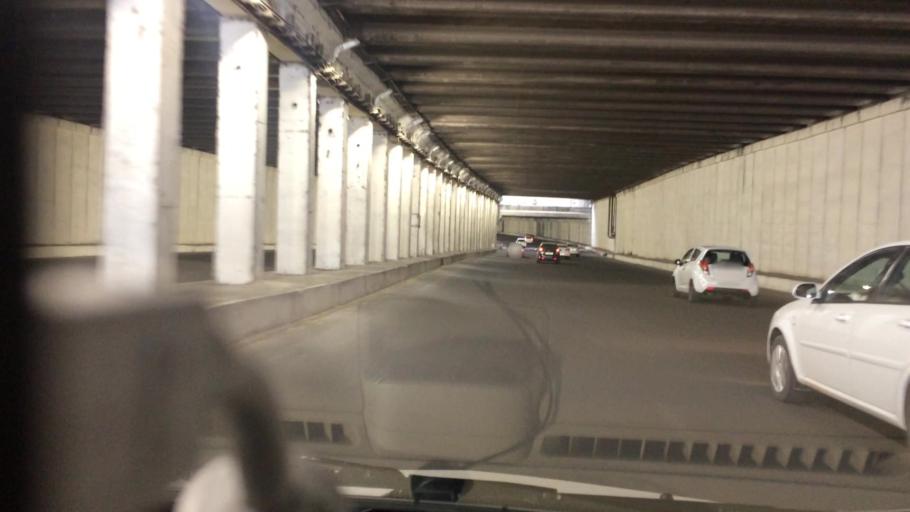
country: UZ
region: Toshkent Shahri
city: Tashkent
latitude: 41.2910
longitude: 69.2844
